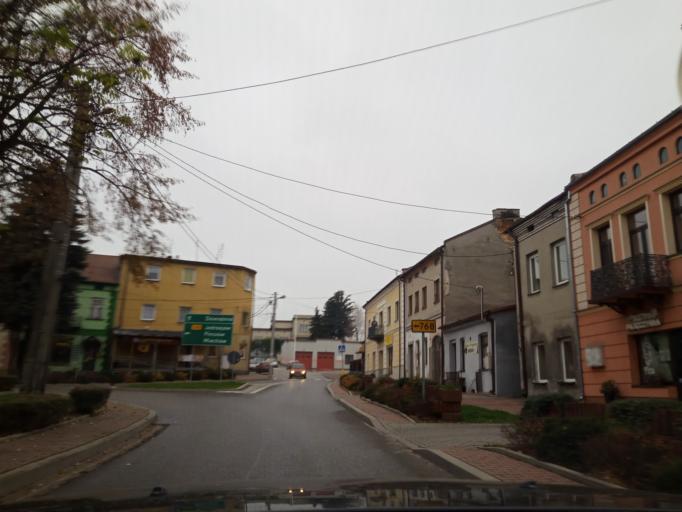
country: PL
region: Swietokrzyskie
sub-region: Powiat pinczowski
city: Dzialoszyce
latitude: 50.3655
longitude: 20.3525
